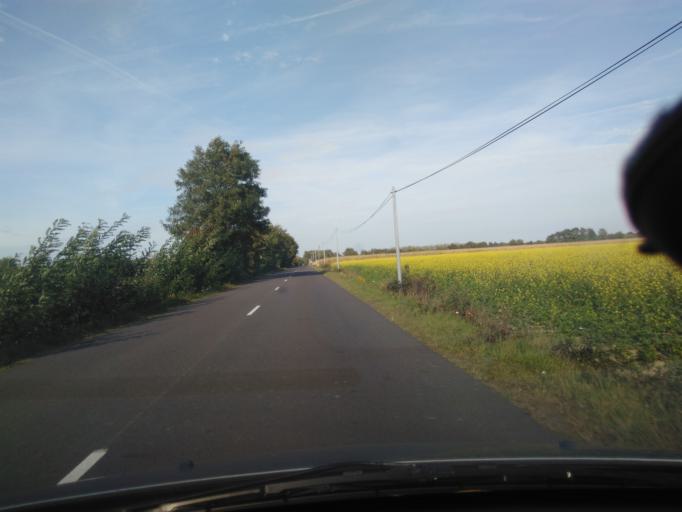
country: FR
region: Pays de la Loire
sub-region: Departement de la Vendee
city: Nieul-le-Dolent
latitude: 46.5349
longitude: -1.5418
